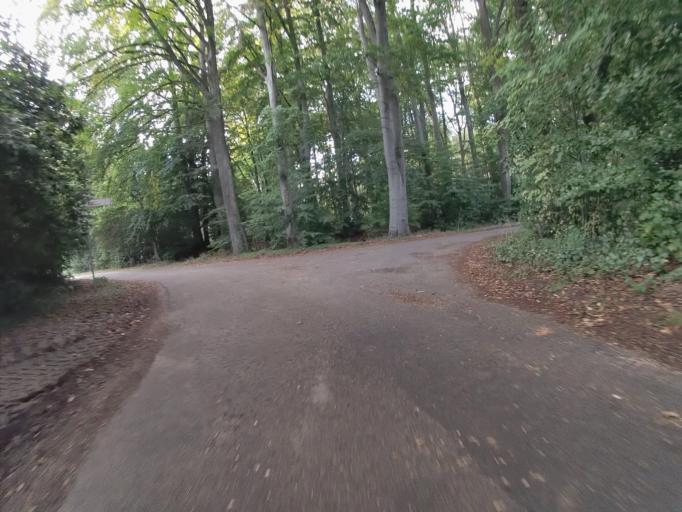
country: DE
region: North Rhine-Westphalia
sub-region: Regierungsbezirk Munster
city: Westerkappeln
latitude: 52.3524
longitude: 7.8949
